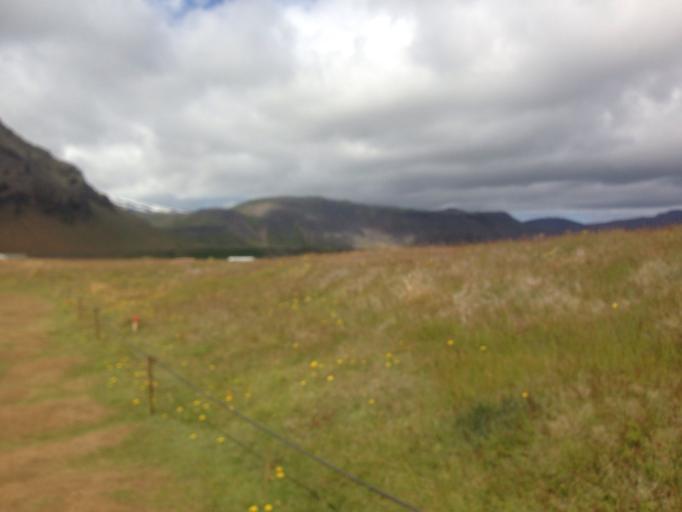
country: IS
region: West
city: Olafsvik
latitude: 64.7655
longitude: -23.6229
